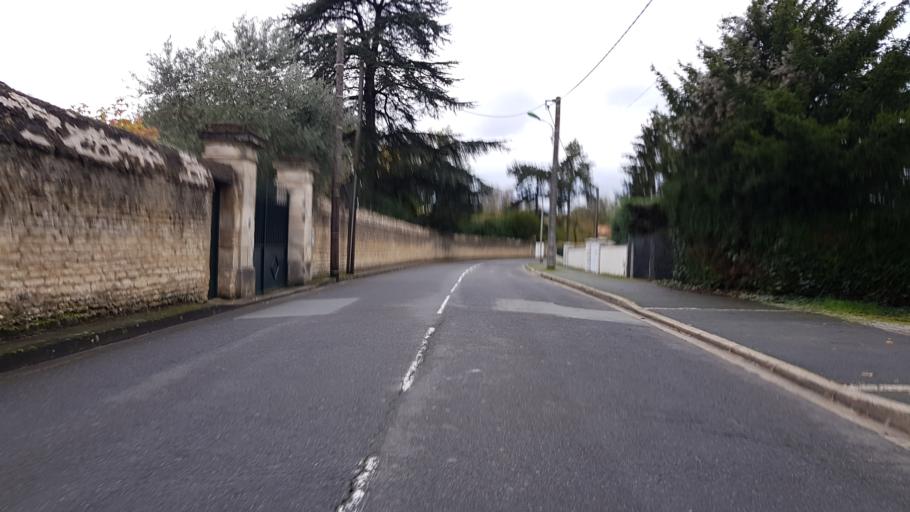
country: FR
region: Poitou-Charentes
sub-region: Departement de la Vienne
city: Chasseneuil-du-Poitou
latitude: 46.6541
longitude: 0.3796
